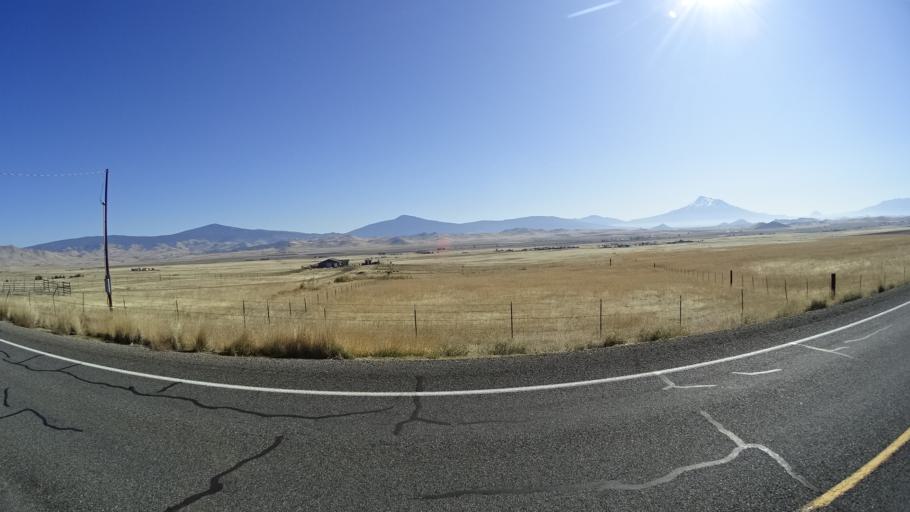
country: US
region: California
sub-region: Siskiyou County
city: Montague
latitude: 41.7943
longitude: -122.5123
